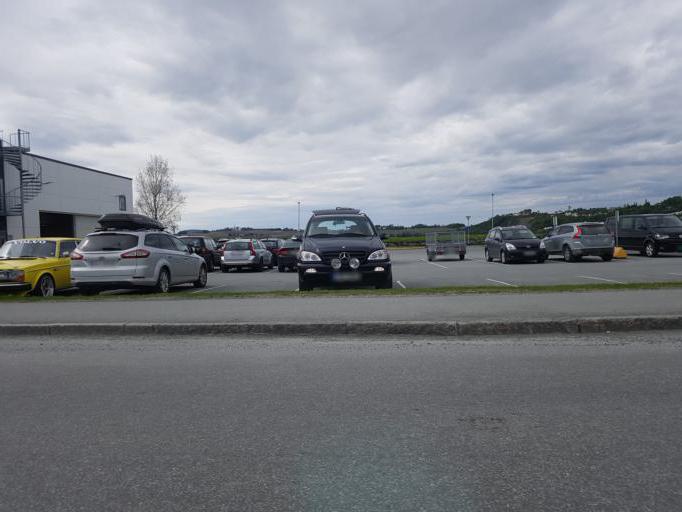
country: NO
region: Nord-Trondelag
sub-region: Levanger
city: Levanger
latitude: 63.7343
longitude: 11.2818
